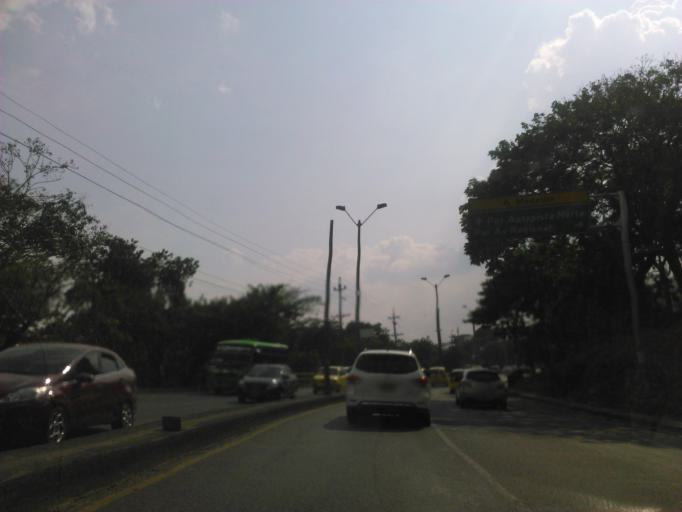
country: CO
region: Antioquia
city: Bello
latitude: 6.3038
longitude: -75.5610
